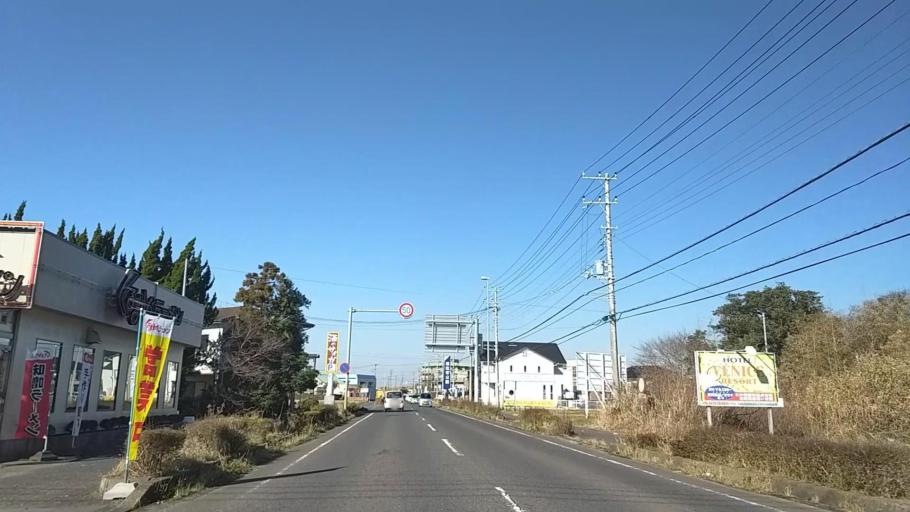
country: JP
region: Chiba
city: Asahi
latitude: 35.7234
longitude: 140.6742
